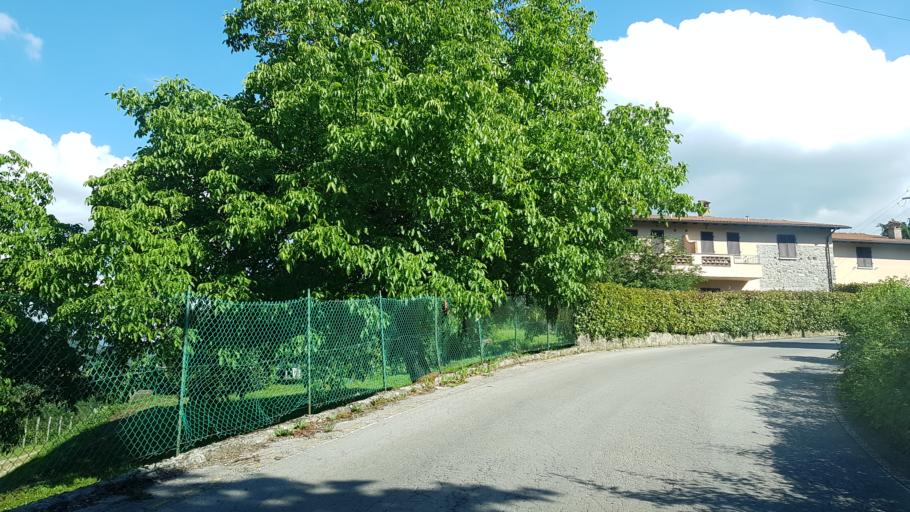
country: IT
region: Tuscany
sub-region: Provincia di Lucca
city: Camporgiano
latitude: 44.1619
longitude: 10.3378
